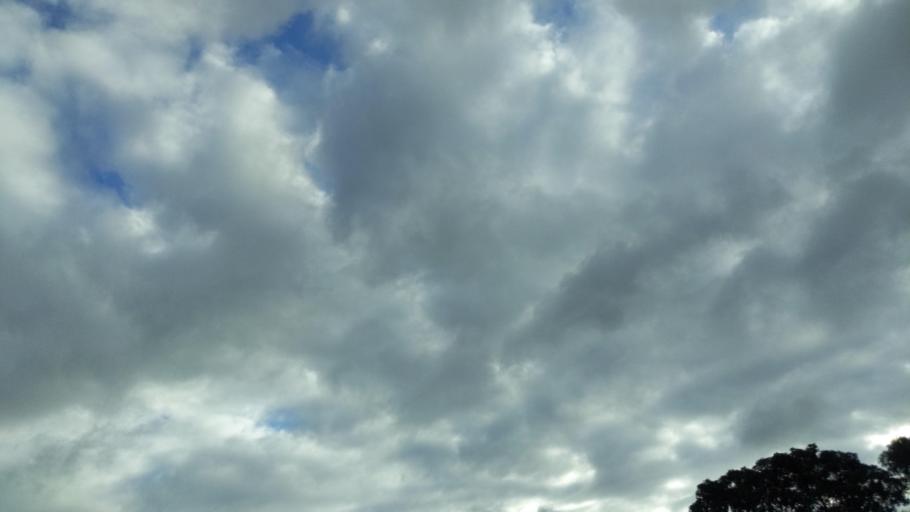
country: AU
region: New South Wales
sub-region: Wagga Wagga
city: Forest Hill
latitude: -35.1612
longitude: 147.5075
